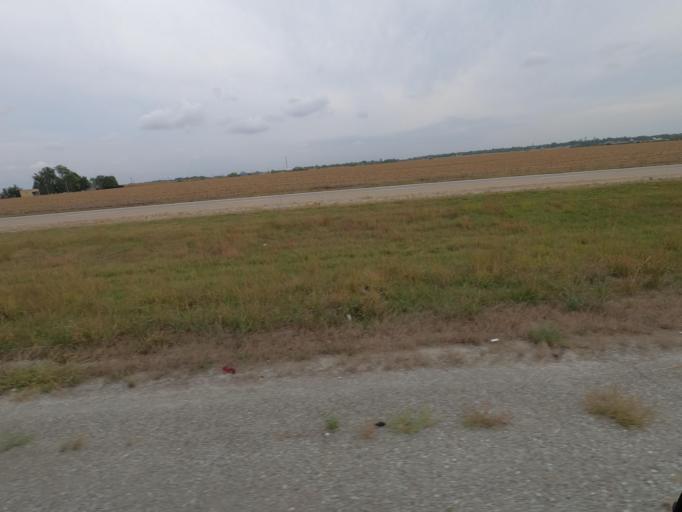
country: US
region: Iowa
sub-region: Jasper County
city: Monroe
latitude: 41.5348
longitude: -93.1304
